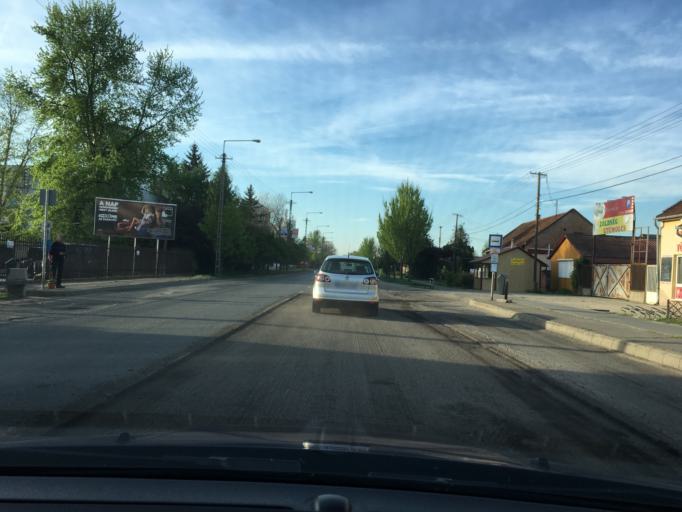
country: HU
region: Hajdu-Bihar
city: Berettyoujfalu
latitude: 47.2118
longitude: 21.5367
